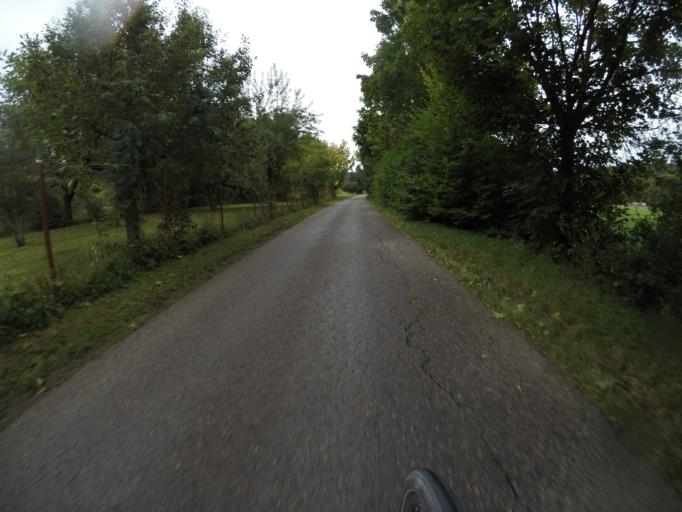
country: DE
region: Baden-Wuerttemberg
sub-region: Regierungsbezirk Stuttgart
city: Leonberg
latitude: 48.7800
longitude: 9.0280
